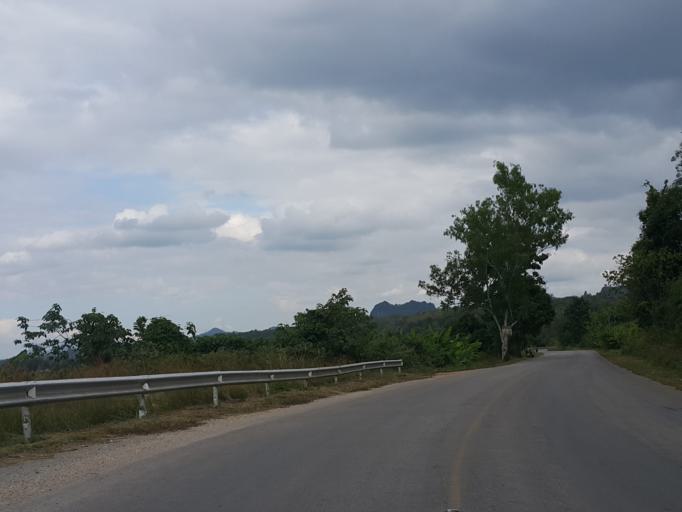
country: TH
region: Lampang
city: Chae Hom
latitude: 18.5903
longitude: 99.4723
